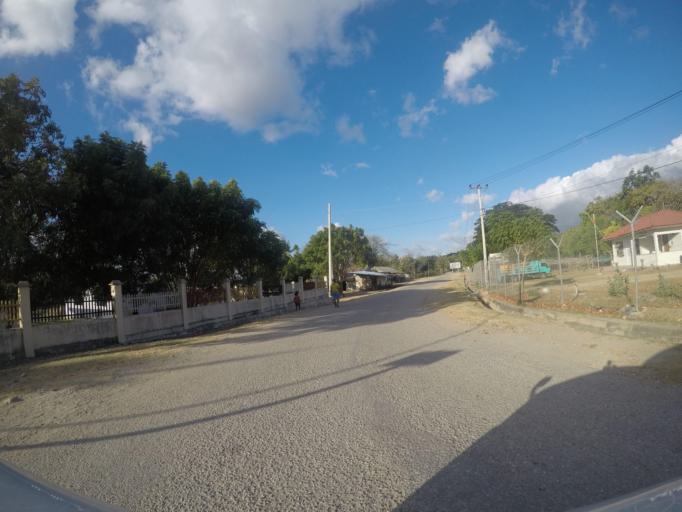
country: TL
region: Lautem
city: Lospalos
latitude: -8.3640
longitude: 126.9020
